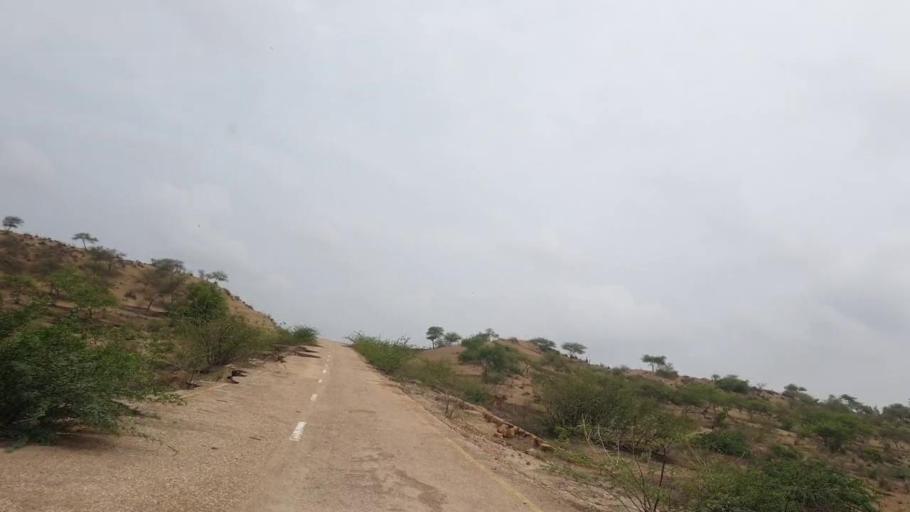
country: PK
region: Sindh
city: Naukot
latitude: 24.6306
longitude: 69.3551
